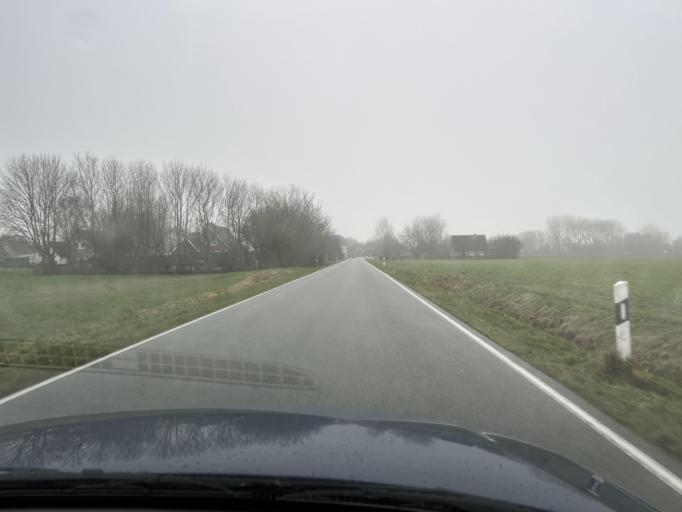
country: DE
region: Schleswig-Holstein
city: Wesselburenerkoog
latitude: 54.2413
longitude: 8.8802
